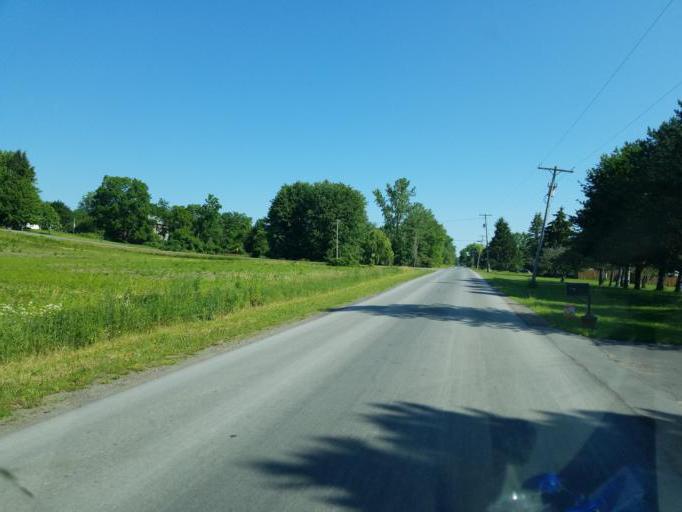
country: US
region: New York
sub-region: Wayne County
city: Clyde
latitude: 43.0443
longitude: -76.8837
